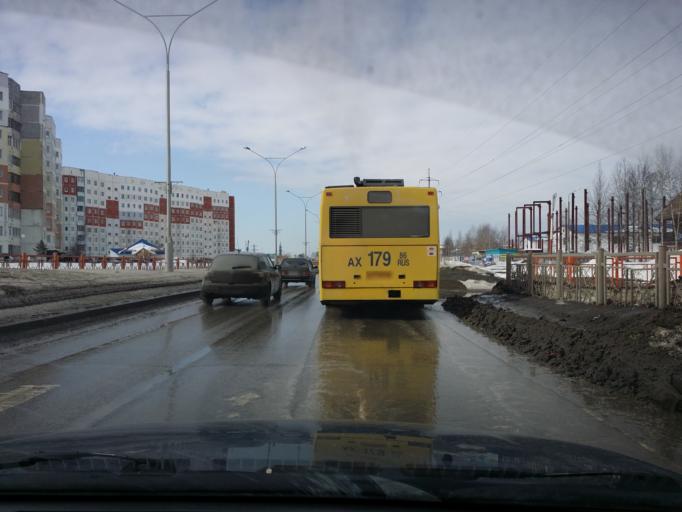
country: RU
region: Khanty-Mansiyskiy Avtonomnyy Okrug
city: Nizhnevartovsk
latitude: 60.9573
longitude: 76.5697
